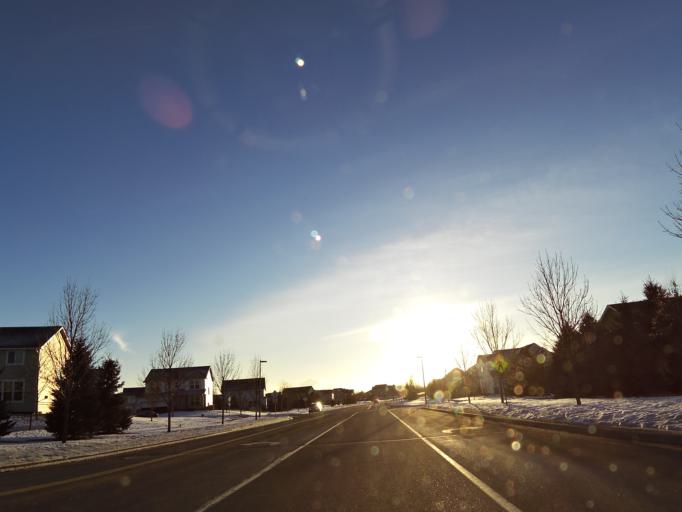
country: US
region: Minnesota
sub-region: Washington County
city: Woodbury
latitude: 44.8983
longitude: -92.8762
